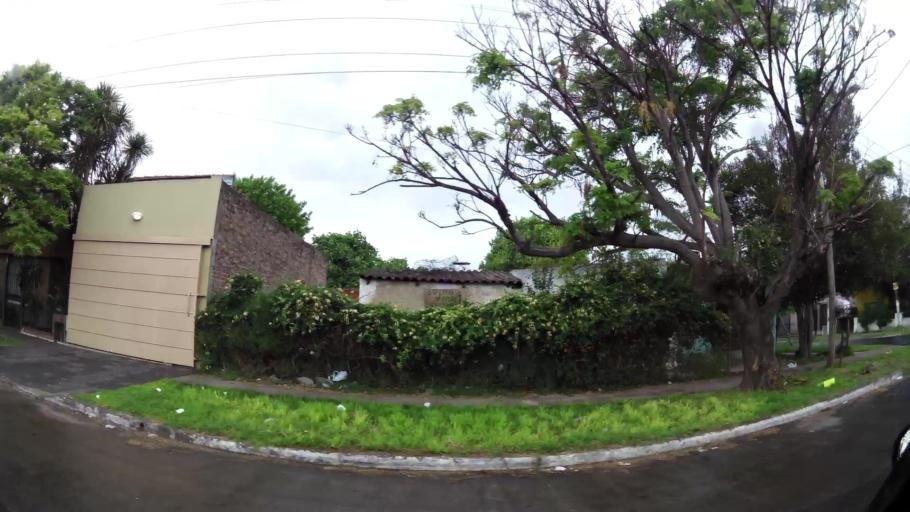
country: AR
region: Buenos Aires
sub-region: Partido de Quilmes
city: Quilmes
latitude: -34.7716
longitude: -58.2177
